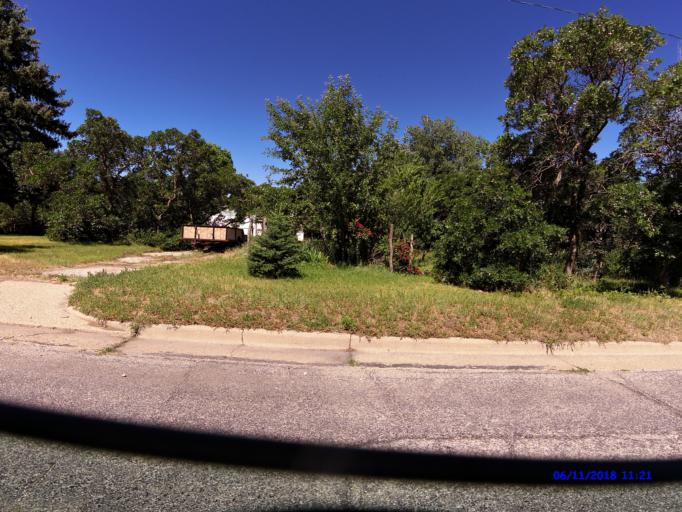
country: US
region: Utah
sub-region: Weber County
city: Ogden
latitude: 41.2225
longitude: -111.9318
